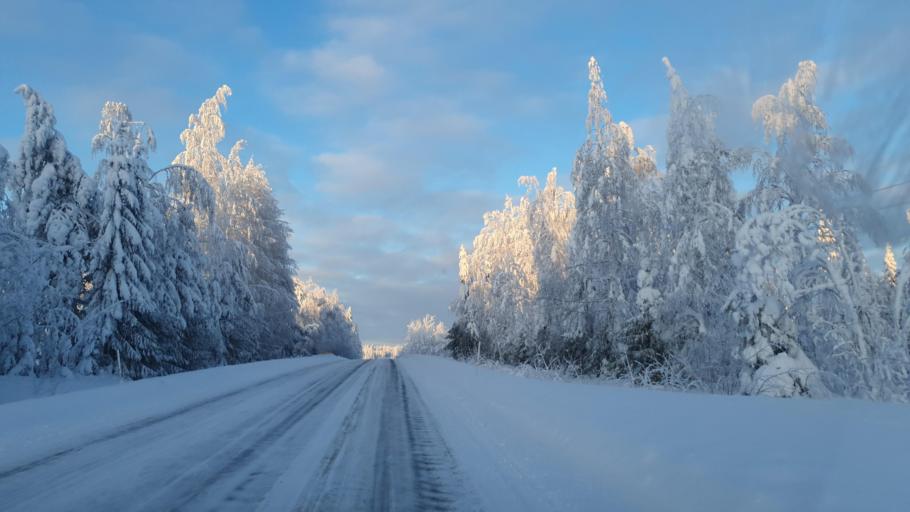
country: FI
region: Kainuu
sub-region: Kajaani
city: Vuokatti
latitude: 64.2354
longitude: 28.2360
